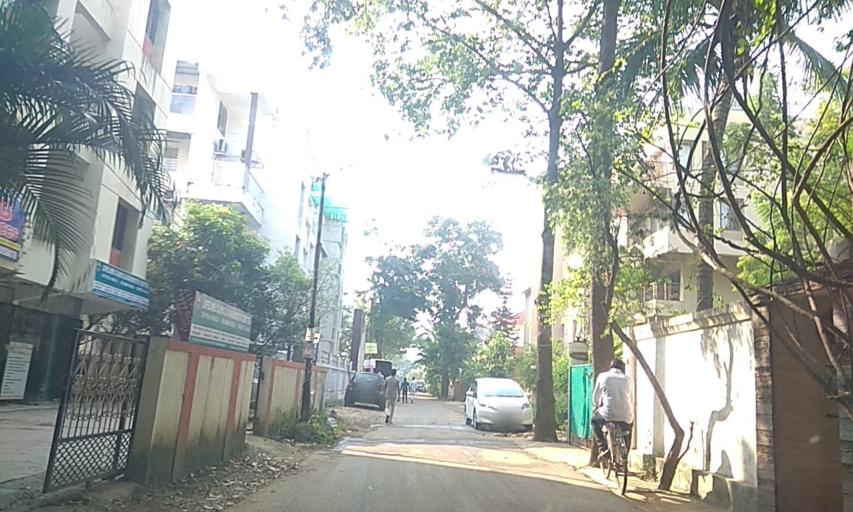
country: IN
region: Maharashtra
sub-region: Pune Division
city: Pimpri
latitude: 18.5634
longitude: 73.7804
